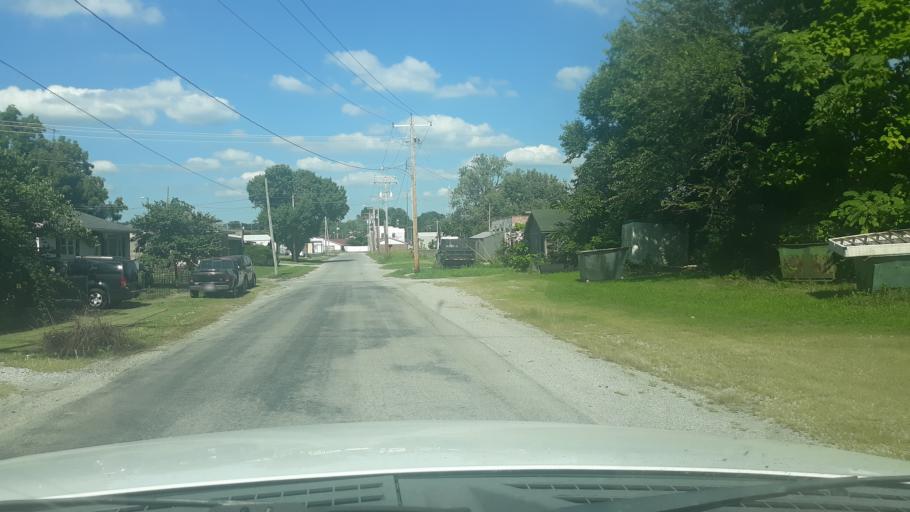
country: US
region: Illinois
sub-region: Saline County
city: Eldorado
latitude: 37.8112
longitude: -88.4414
